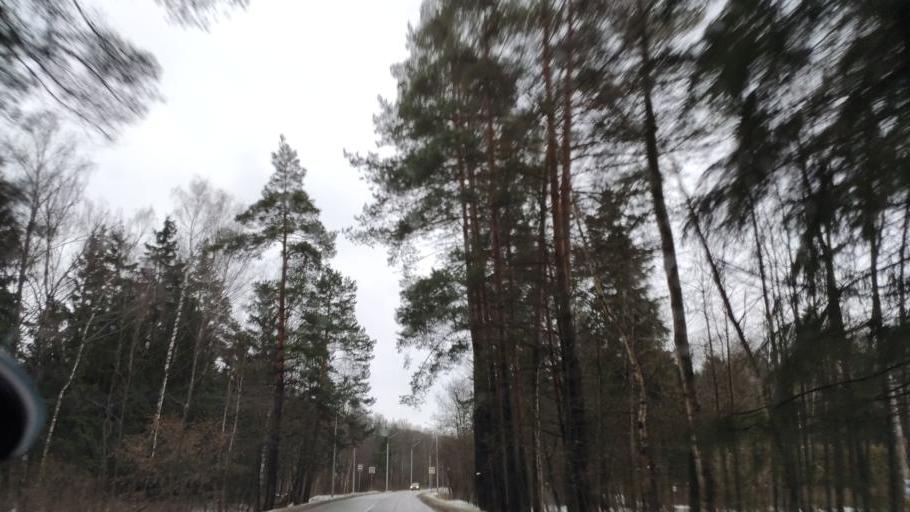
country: RU
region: Moskovskaya
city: Dubrovitsy
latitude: 55.4320
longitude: 37.3990
